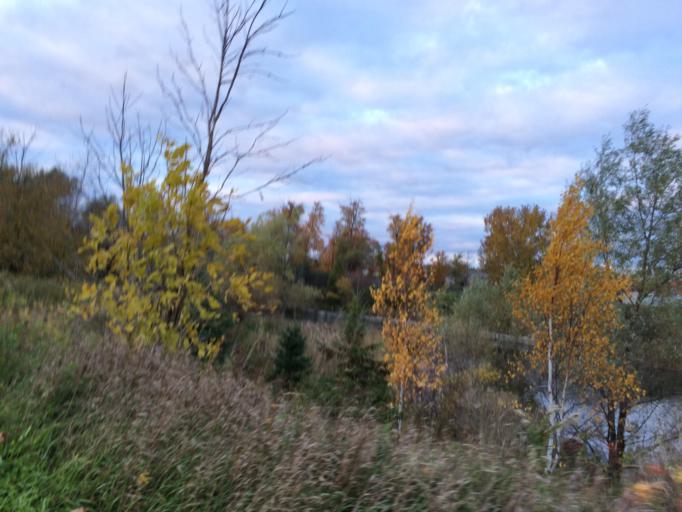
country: CA
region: Ontario
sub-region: Wellington County
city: Guelph
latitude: 43.5253
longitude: -80.2960
